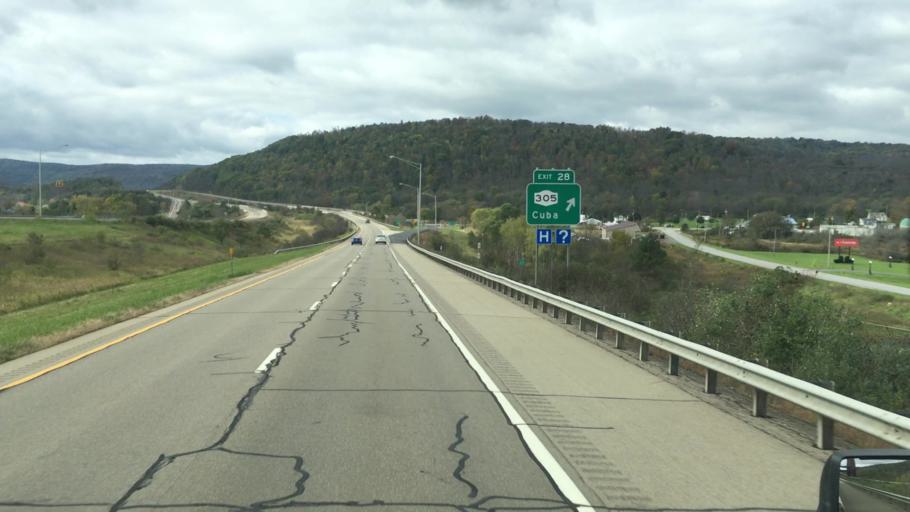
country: US
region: New York
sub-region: Allegany County
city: Cuba
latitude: 42.2253
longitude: -78.2700
